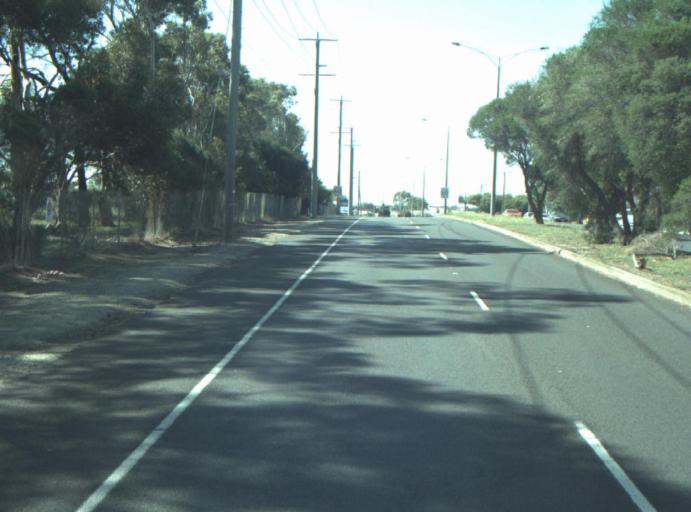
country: AU
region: Victoria
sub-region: Greater Geelong
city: Geelong West
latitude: -38.1288
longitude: 144.3410
